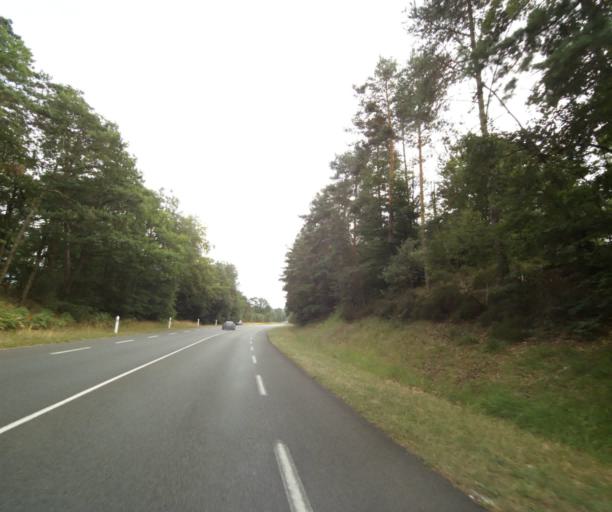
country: FR
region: Ile-de-France
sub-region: Departement de Seine-et-Marne
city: Bois-le-Roi
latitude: 48.4492
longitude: 2.6877
